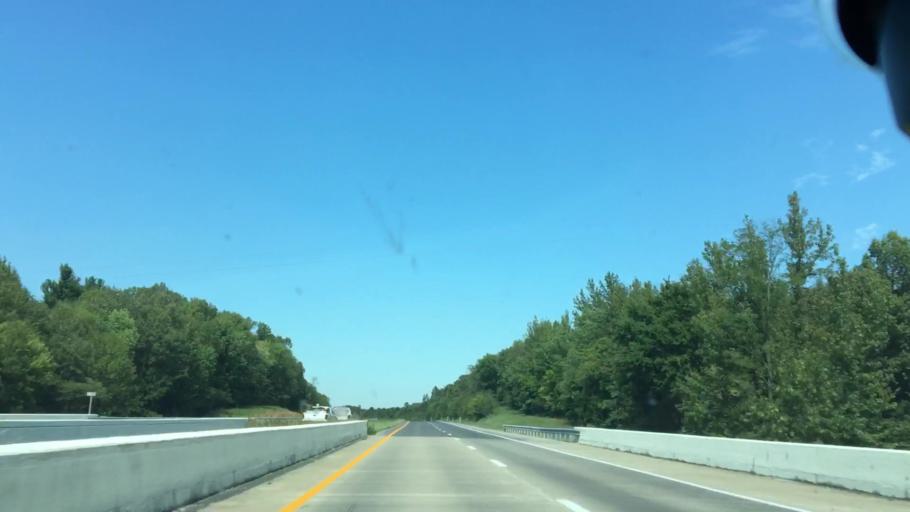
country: US
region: Kentucky
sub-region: Webster County
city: Sebree
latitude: 37.5255
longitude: -87.4754
